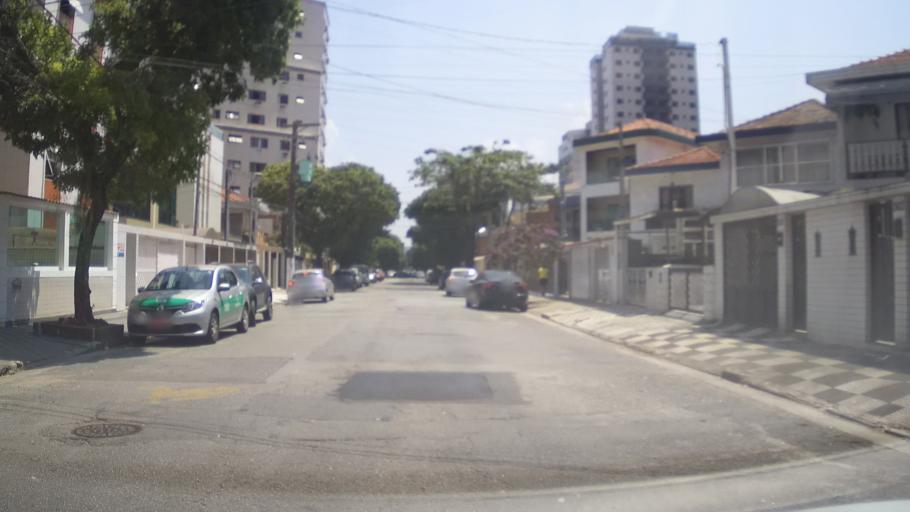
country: BR
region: Sao Paulo
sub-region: Santos
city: Santos
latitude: -23.9705
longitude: -46.3062
